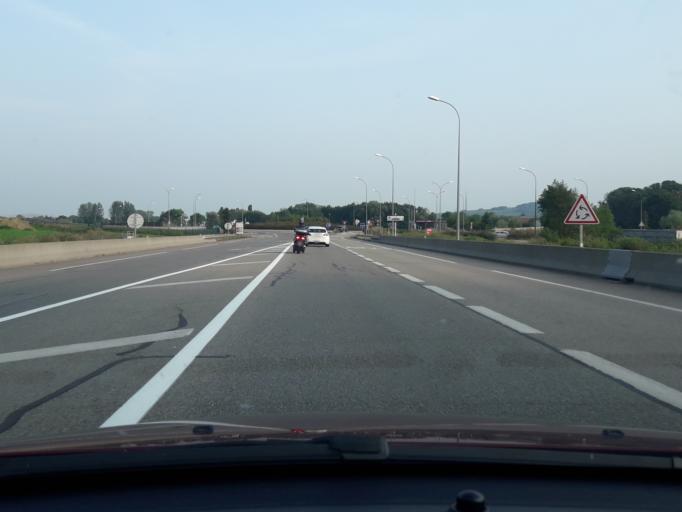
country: FR
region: Alsace
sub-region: Departement du Bas-Rhin
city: Marlenheim
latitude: 48.6231
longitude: 7.4738
